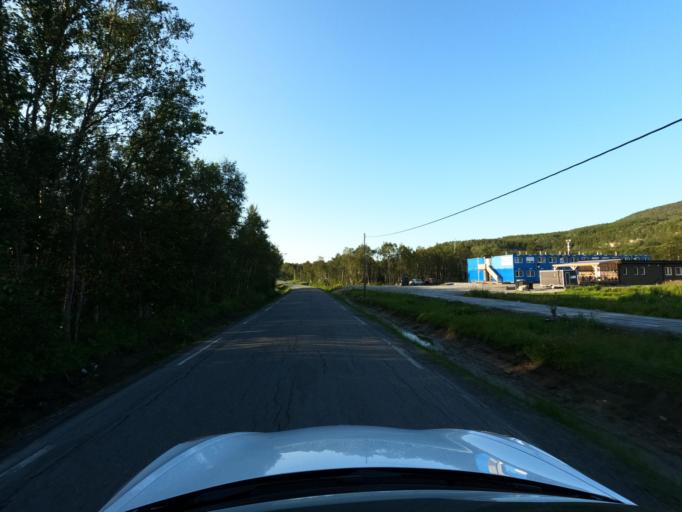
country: NO
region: Troms
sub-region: Skanland
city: Evenskjer
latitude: 68.4724
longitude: 16.7047
